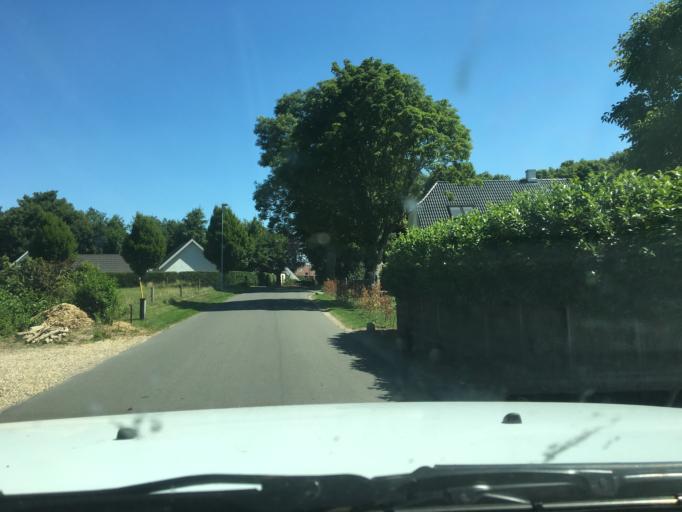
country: DK
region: Central Jutland
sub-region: Horsens Kommune
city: Braedstrup
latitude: 55.9468
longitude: 9.5628
